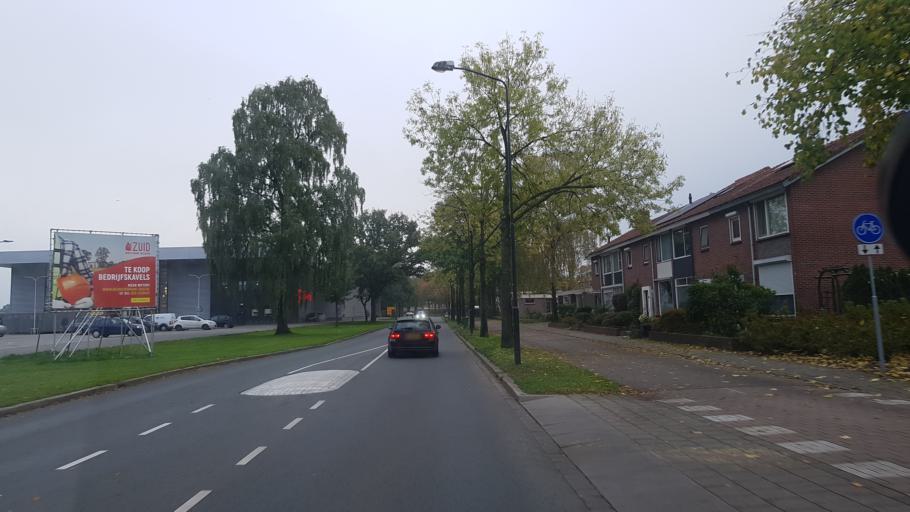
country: NL
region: Gelderland
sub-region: Gemeente Apeldoorn
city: Apeldoorn
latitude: 52.1975
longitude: 5.9791
